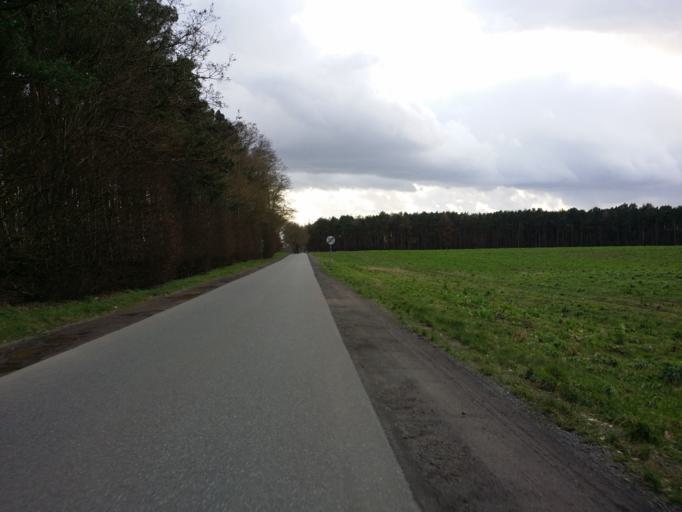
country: DE
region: Lower Saxony
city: Gross Ippener
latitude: 52.9978
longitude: 8.6430
